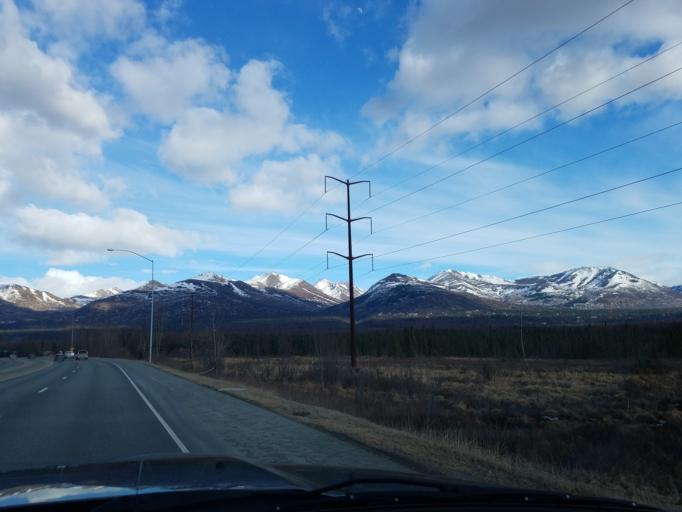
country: US
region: Alaska
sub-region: Anchorage Municipality
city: Elmendorf Air Force Base
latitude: 61.1807
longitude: -149.7470
